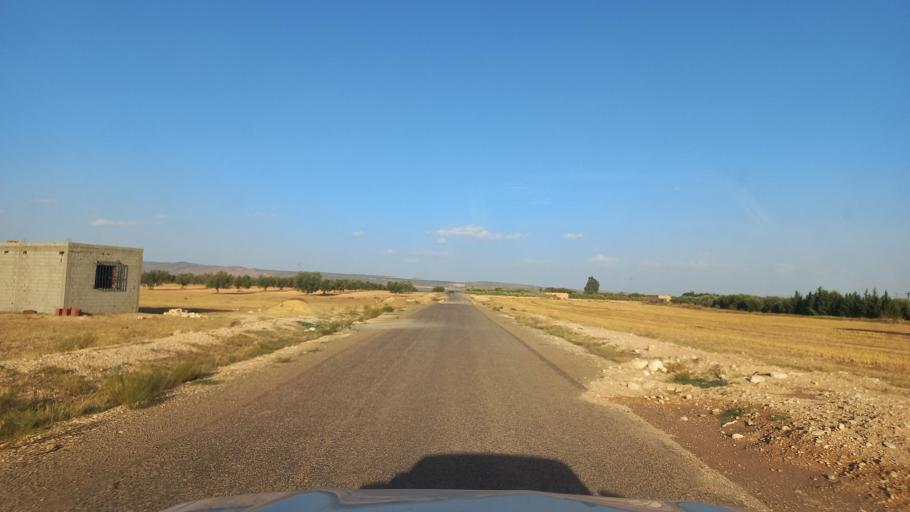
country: TN
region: Al Qasrayn
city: Kasserine
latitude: 35.2869
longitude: 9.0317
